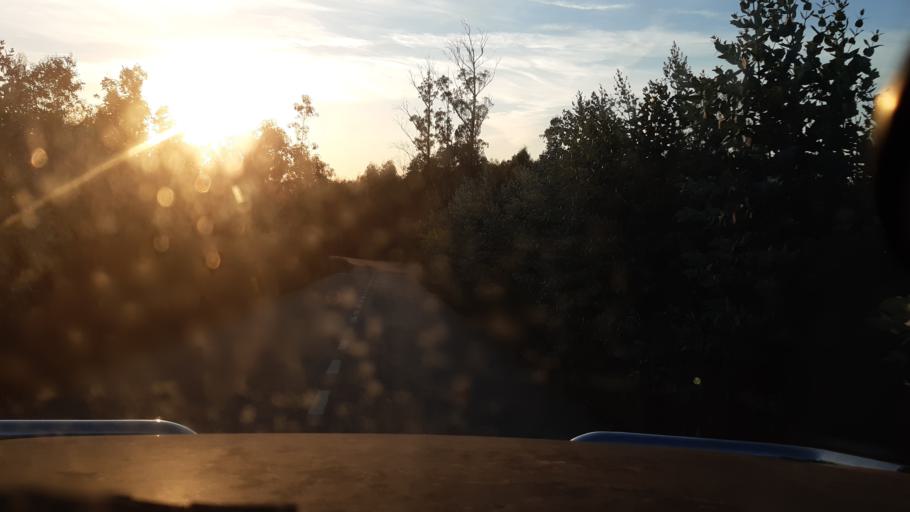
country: PT
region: Aveiro
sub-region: Agueda
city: Aguada de Cima
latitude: 40.5655
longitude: -8.3167
